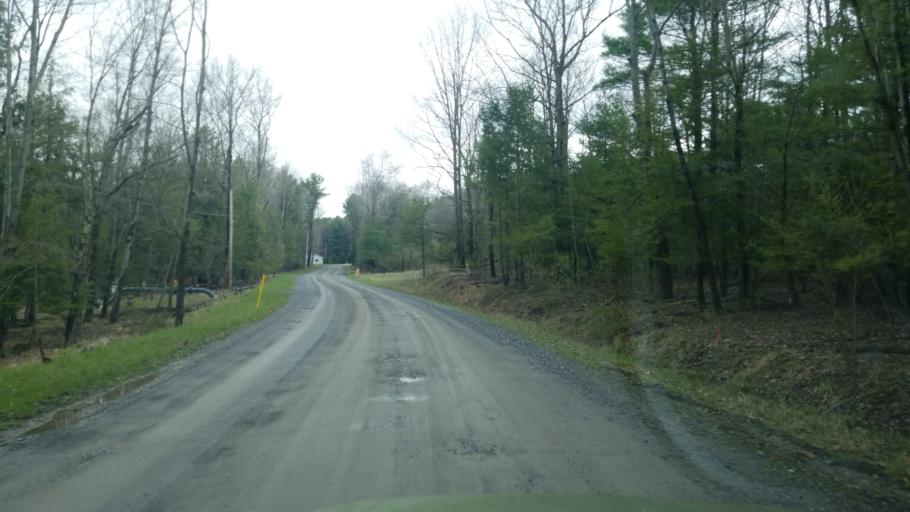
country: US
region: Pennsylvania
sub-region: Clearfield County
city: Shiloh
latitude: 41.1217
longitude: -78.3405
